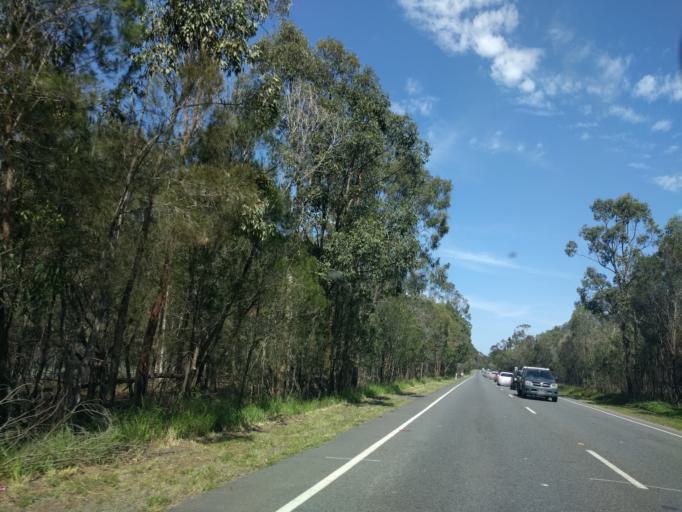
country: AU
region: Queensland
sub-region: Brisbane
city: Forest Lake
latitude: -27.6351
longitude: 152.9621
